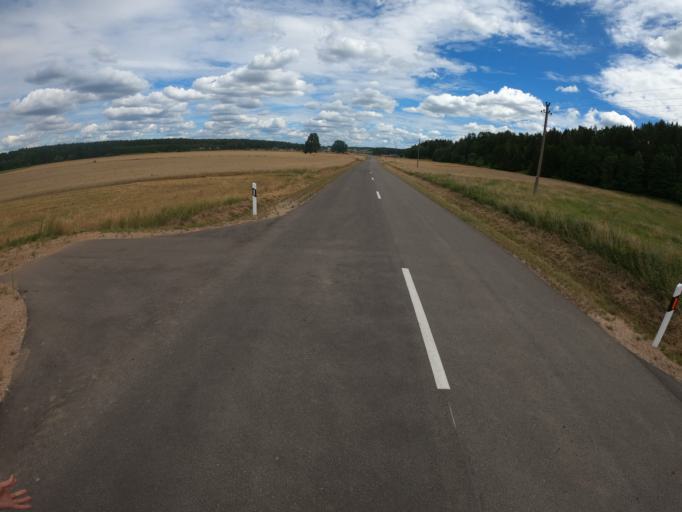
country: LT
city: Prienai
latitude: 54.5442
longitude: 23.9337
